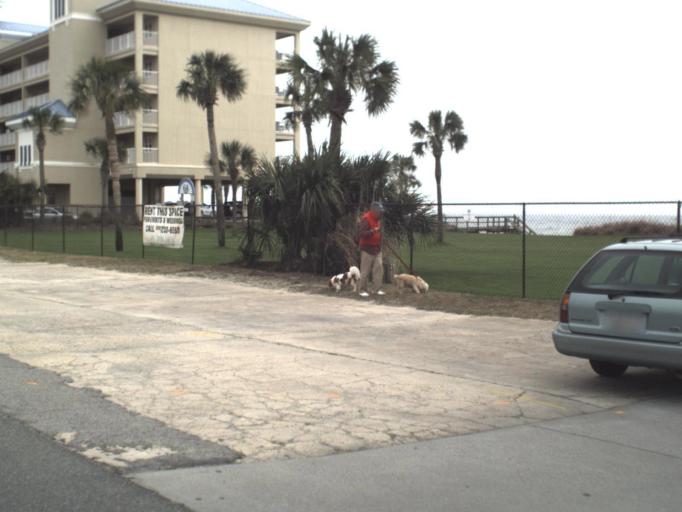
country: US
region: Florida
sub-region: Bay County
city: Laguna Beach
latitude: 30.2220
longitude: -85.8887
